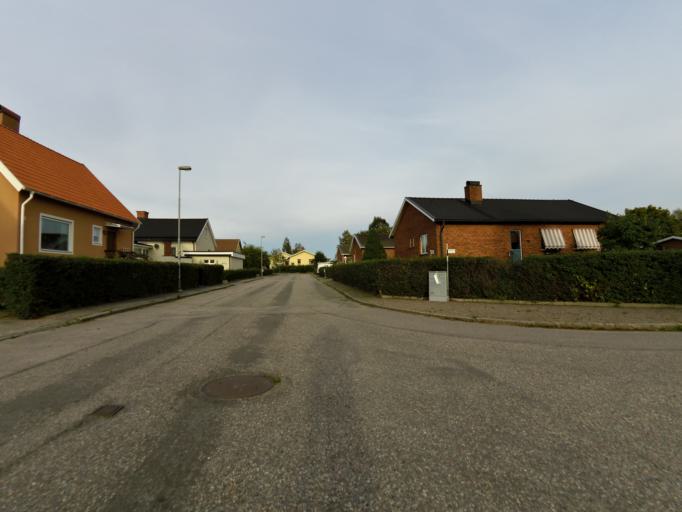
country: SE
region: Gaevleborg
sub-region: Gavle Kommun
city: Gavle
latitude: 60.7013
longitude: 17.1663
